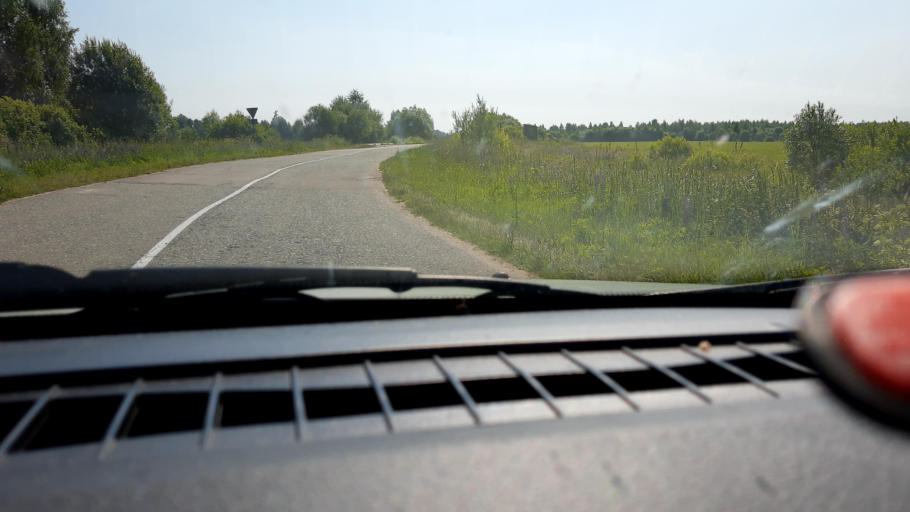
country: RU
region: Nizjnij Novgorod
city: Sharanga
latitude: 57.0272
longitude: 46.5858
